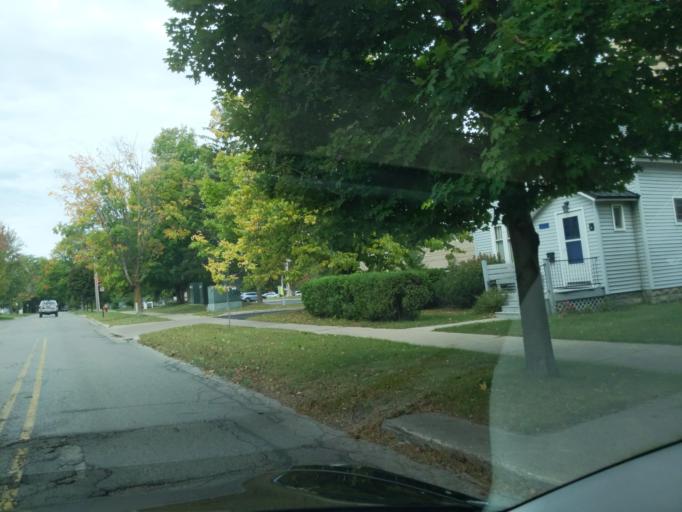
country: US
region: Michigan
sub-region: Grand Traverse County
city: Traverse City
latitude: 44.7618
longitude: -85.6173
